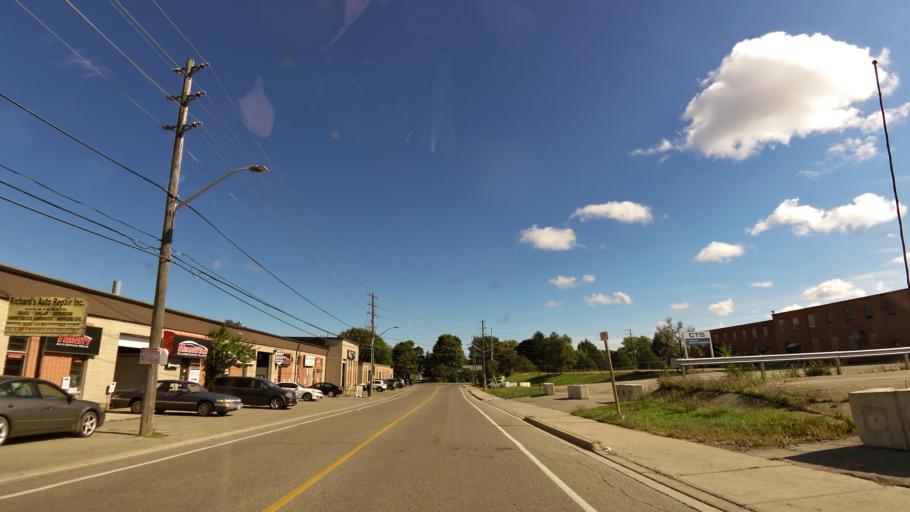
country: CA
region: Ontario
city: Mississauga
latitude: 43.5783
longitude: -79.7166
